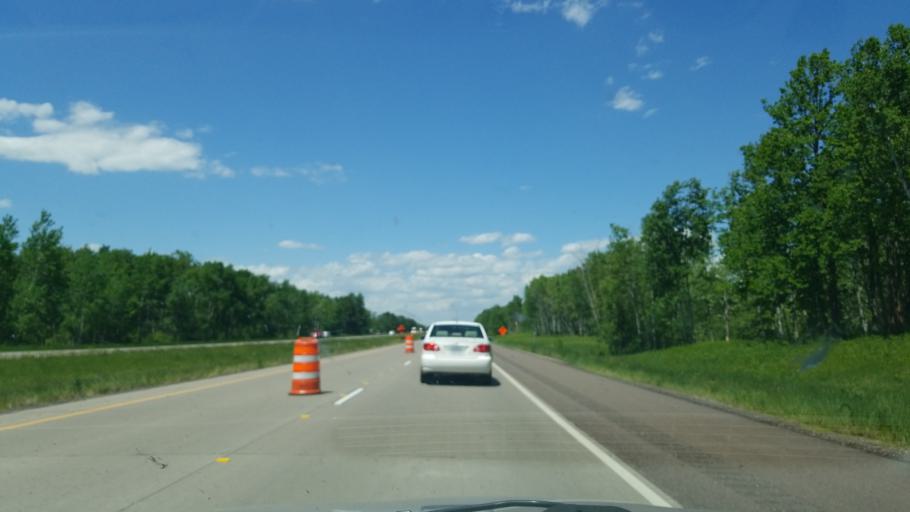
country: US
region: Minnesota
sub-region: Pine County
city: Sandstone
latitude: 46.2618
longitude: -92.8251
